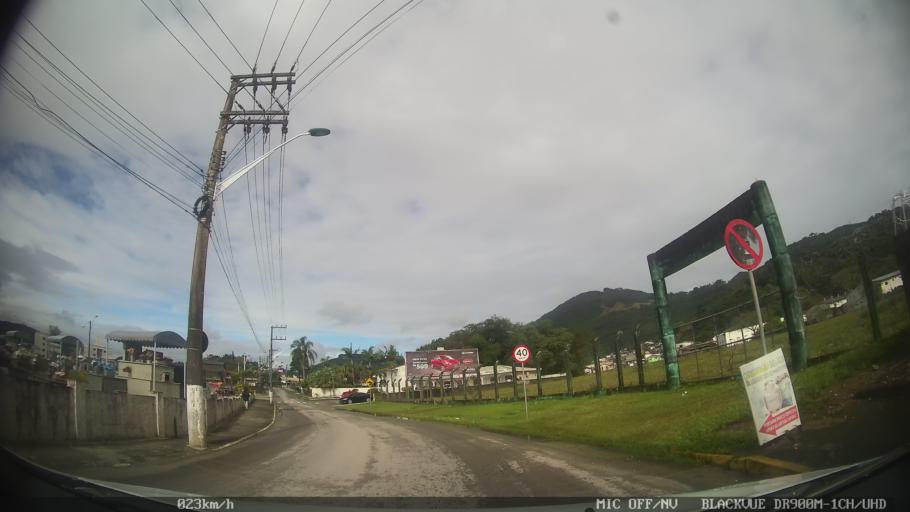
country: BR
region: Santa Catarina
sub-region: Biguacu
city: Biguacu
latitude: -27.5072
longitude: -48.6575
